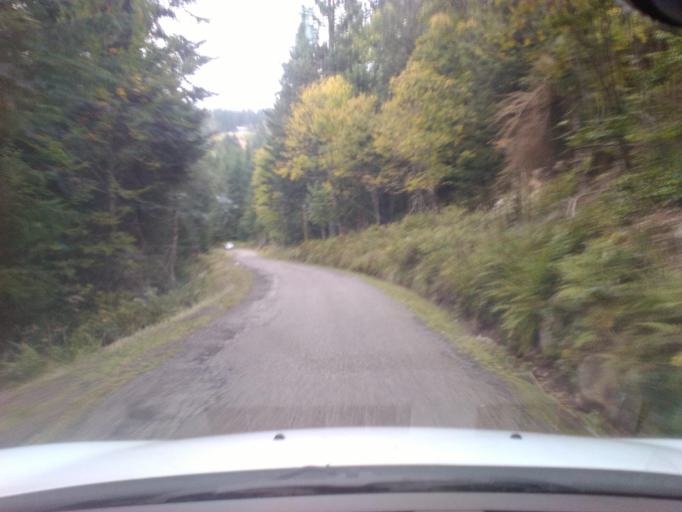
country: FR
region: Lorraine
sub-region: Departement des Vosges
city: Gerardmer
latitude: 48.0485
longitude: 6.8905
